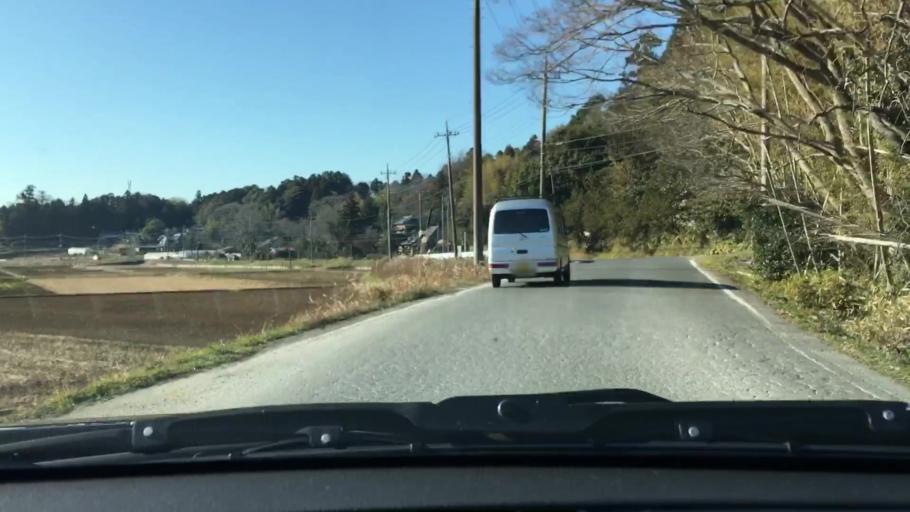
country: JP
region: Chiba
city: Shisui
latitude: 35.7021
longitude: 140.2820
